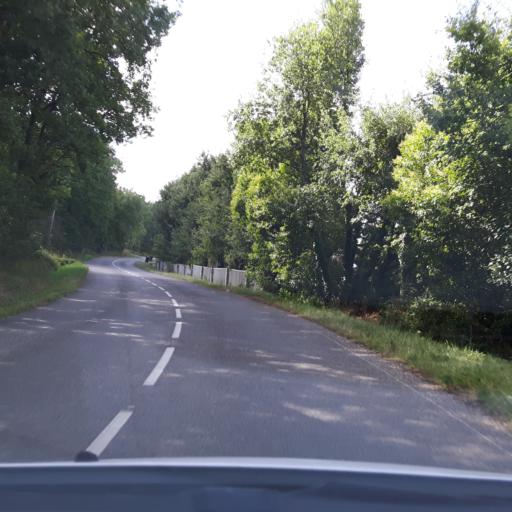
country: FR
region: Midi-Pyrenees
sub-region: Departement de la Haute-Garonne
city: Bouloc
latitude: 43.7958
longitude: 1.4131
